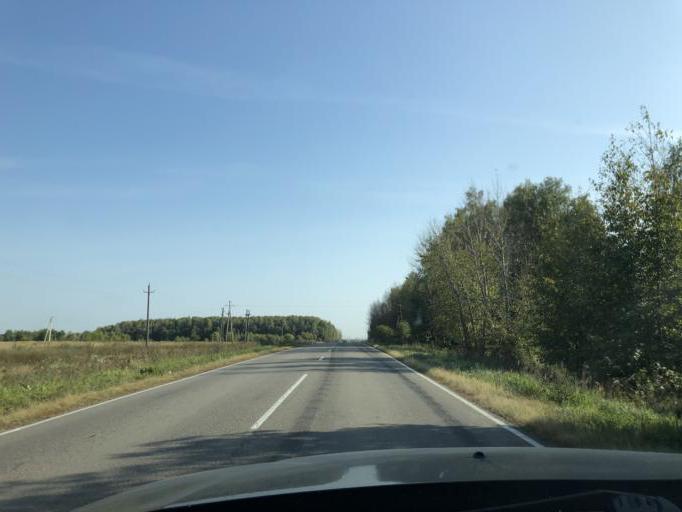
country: RU
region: Tula
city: Novogurovskiy
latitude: 54.4539
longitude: 37.4369
